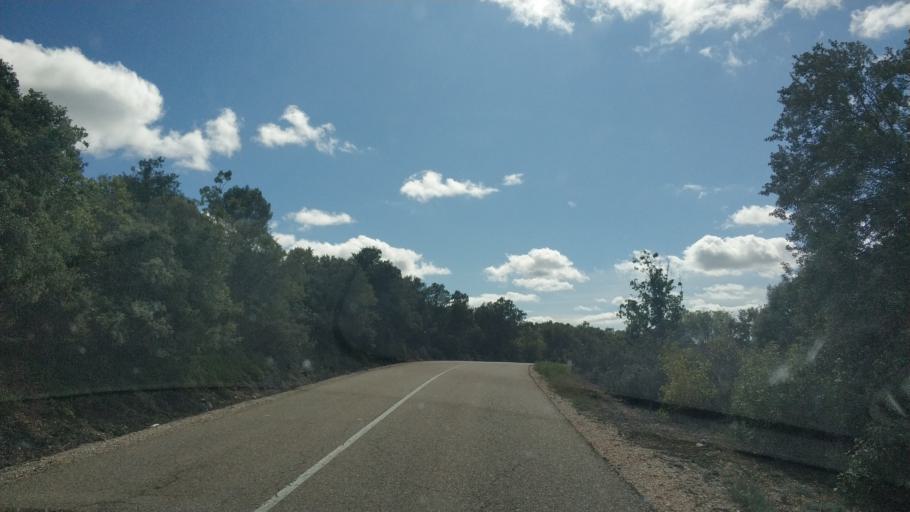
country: ES
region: Castille and Leon
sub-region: Provincia de Burgos
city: Retuerta
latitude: 42.0439
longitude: -3.4938
